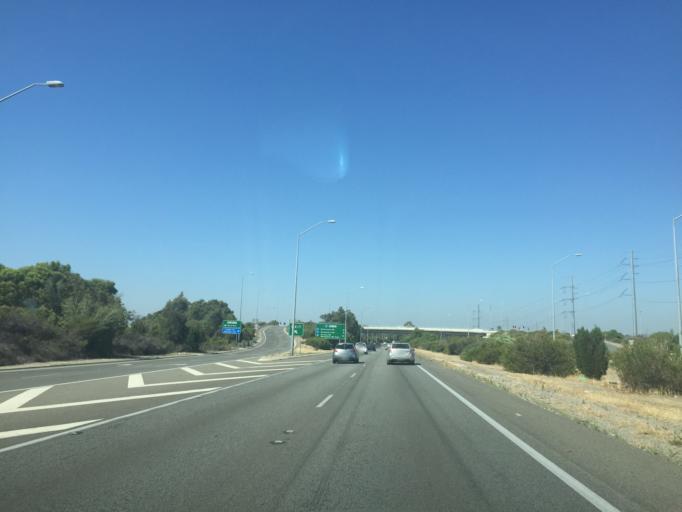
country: AU
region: Western Australia
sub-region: Canning
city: Canning Vale
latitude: -32.0588
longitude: 115.9025
